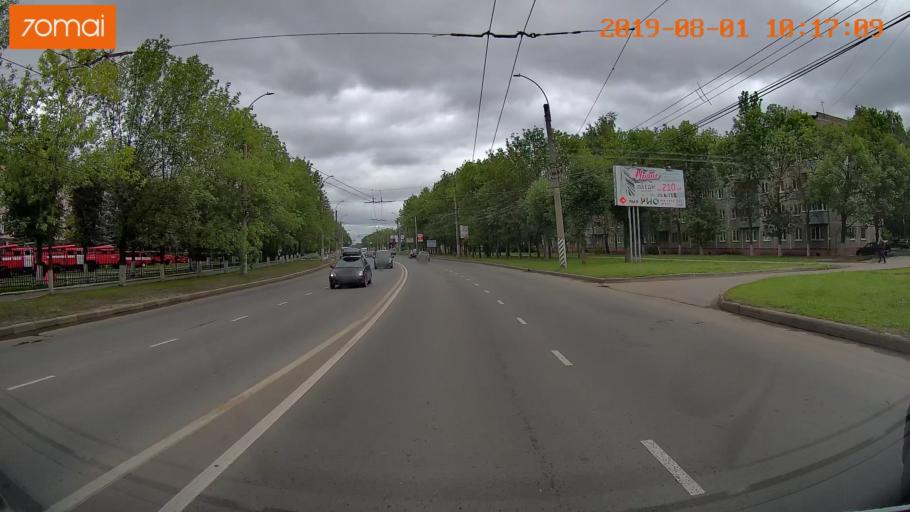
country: RU
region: Ivanovo
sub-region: Gorod Ivanovo
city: Ivanovo
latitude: 56.9636
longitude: 40.9994
